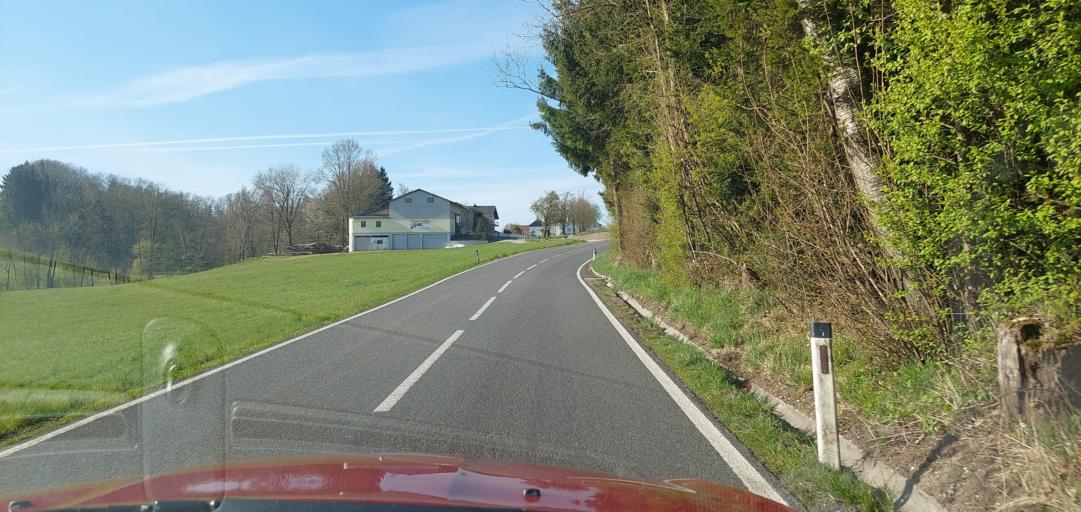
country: AT
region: Upper Austria
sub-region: Politischer Bezirk Ried im Innkreis
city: Ried im Innkreis
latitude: 48.1769
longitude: 13.5428
